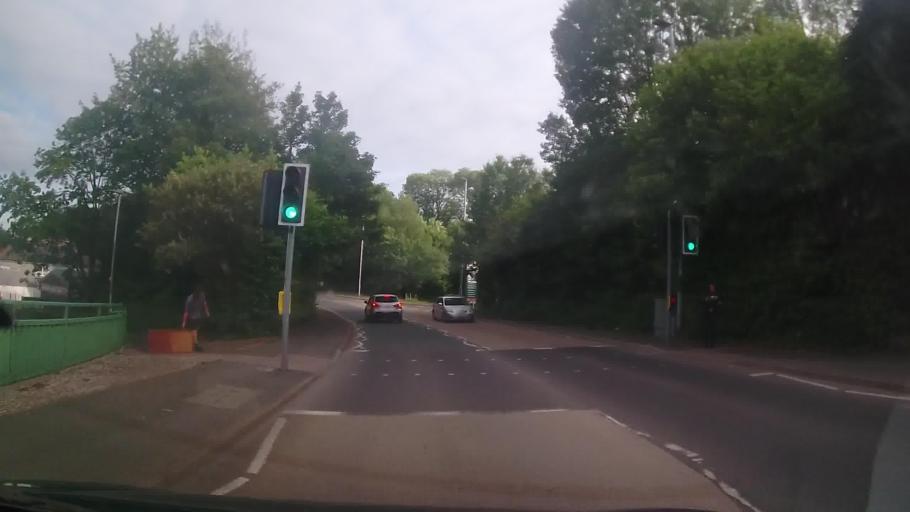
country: GB
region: England
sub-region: Devon
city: Kingsbridge
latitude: 50.2845
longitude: -3.7806
